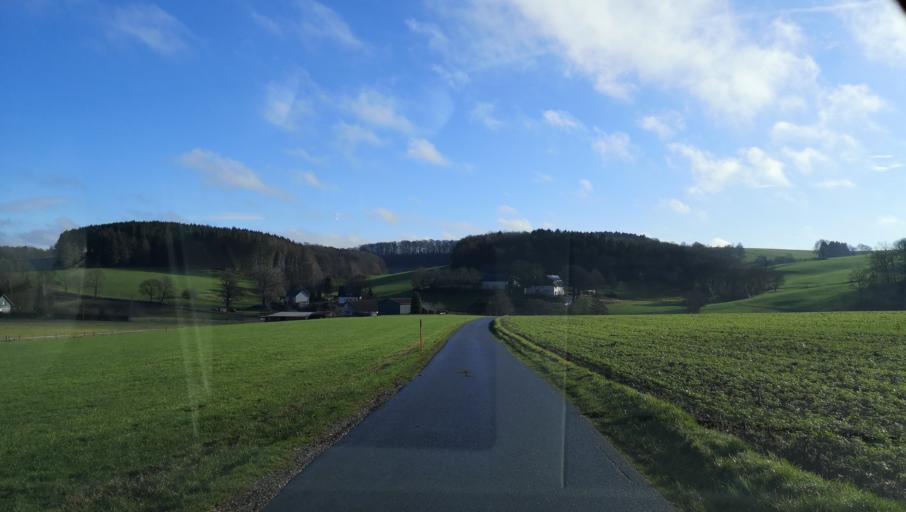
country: DE
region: North Rhine-Westphalia
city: Radevormwald
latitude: 51.1848
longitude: 7.4166
